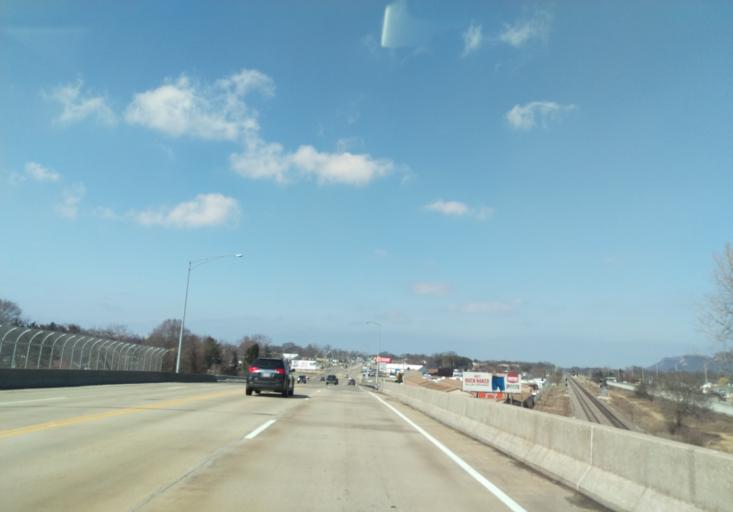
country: US
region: Wisconsin
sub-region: La Crosse County
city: La Crosse
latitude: 43.7620
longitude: -91.2075
